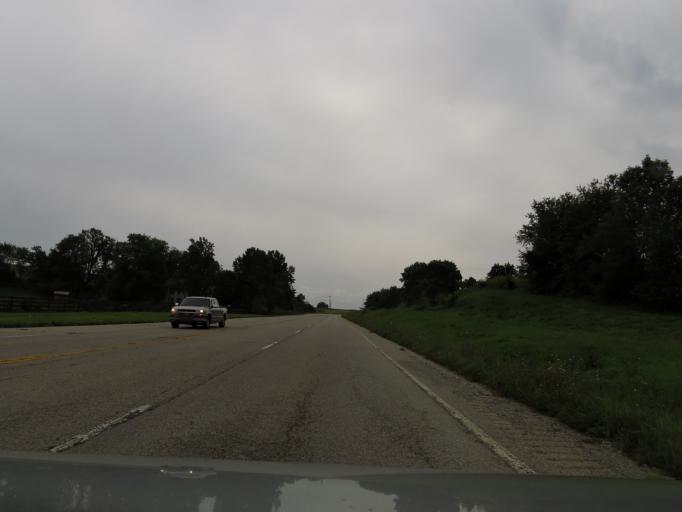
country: US
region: Kentucky
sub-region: Mason County
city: Maysville
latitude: 38.5661
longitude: -83.8233
